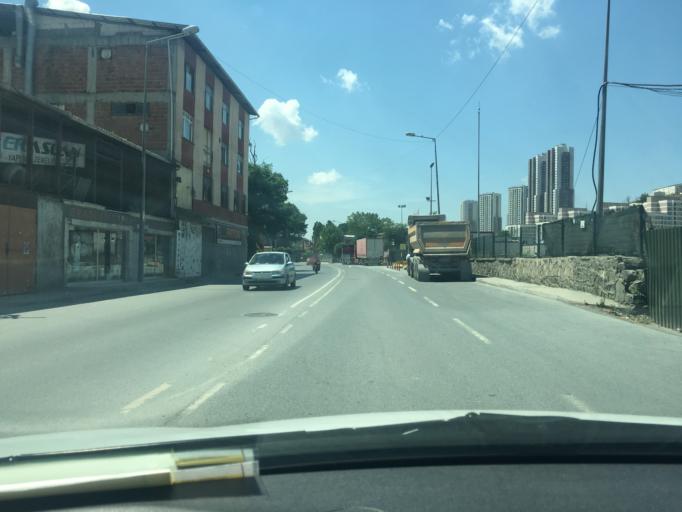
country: TR
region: Istanbul
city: Sisli
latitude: 41.0858
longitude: 28.9459
